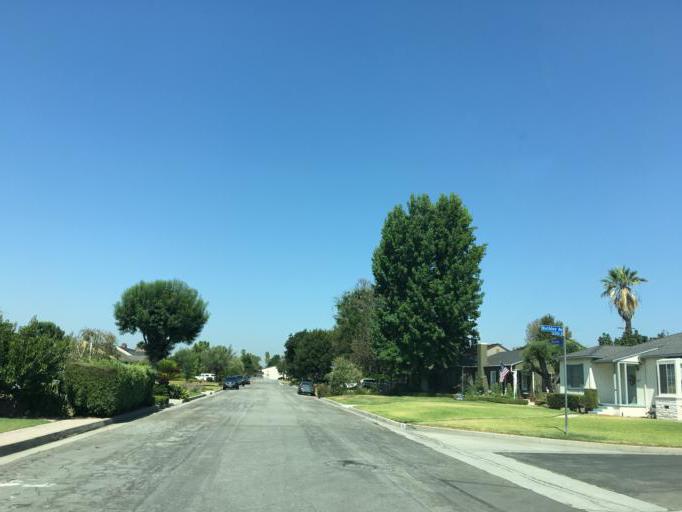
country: US
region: California
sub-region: Los Angeles County
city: San Marino
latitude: 34.1181
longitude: -118.0854
